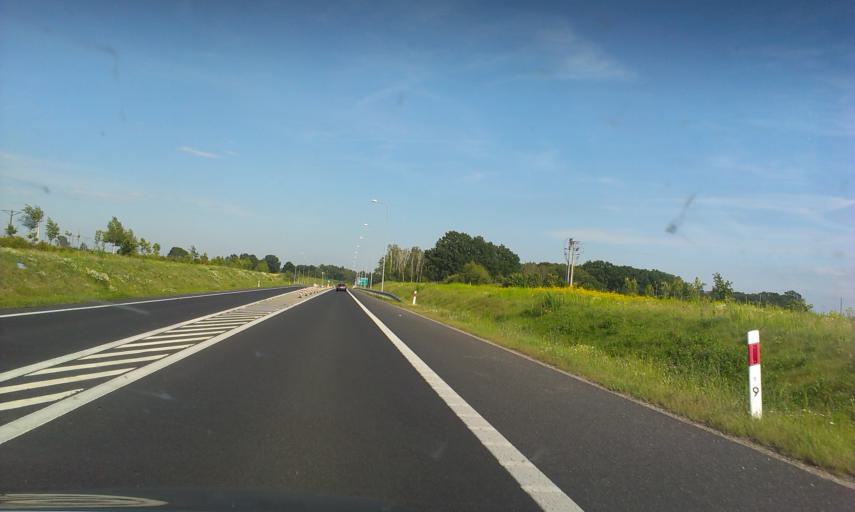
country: PL
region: Greater Poland Voivodeship
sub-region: Powiat pilski
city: Wyrzysk
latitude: 53.1605
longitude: 17.2910
